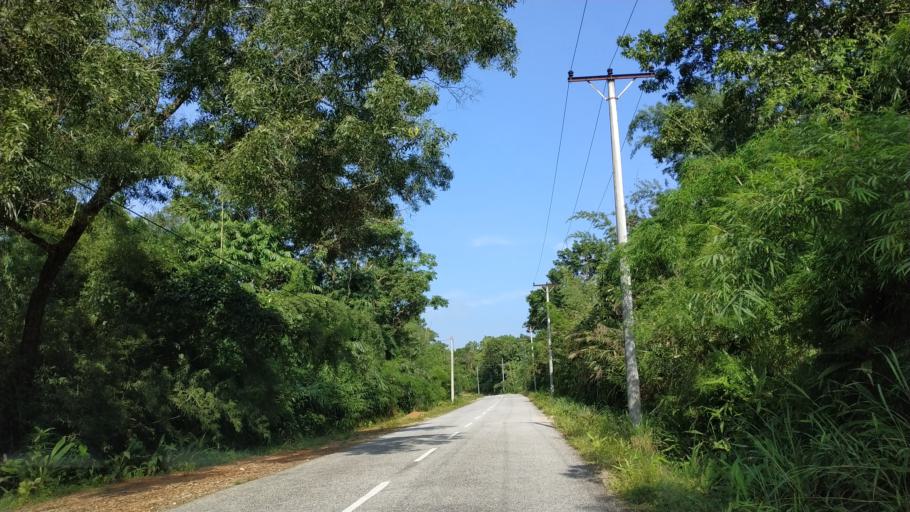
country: TH
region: Kanchanaburi
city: Thong Pha Phum
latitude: 14.6261
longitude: 98.1182
